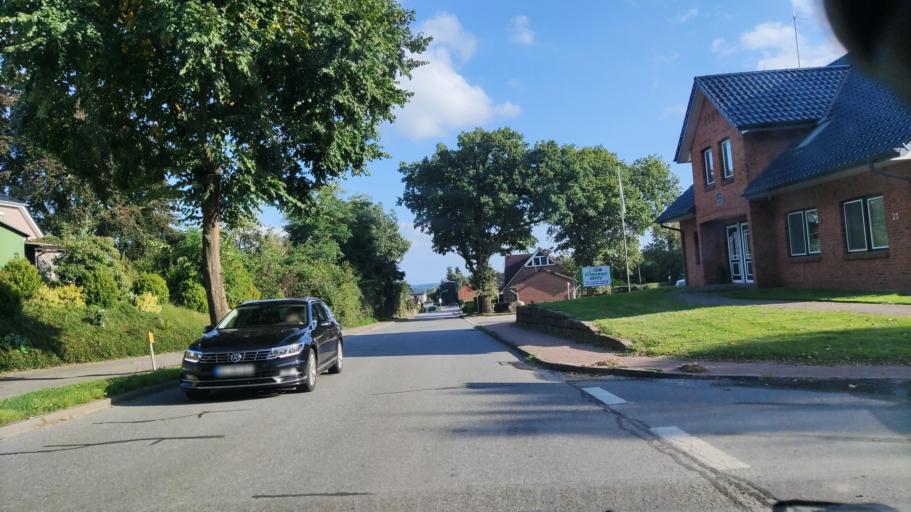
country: DE
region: Schleswig-Holstein
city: Sarlhusen
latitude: 54.0265
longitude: 9.7894
